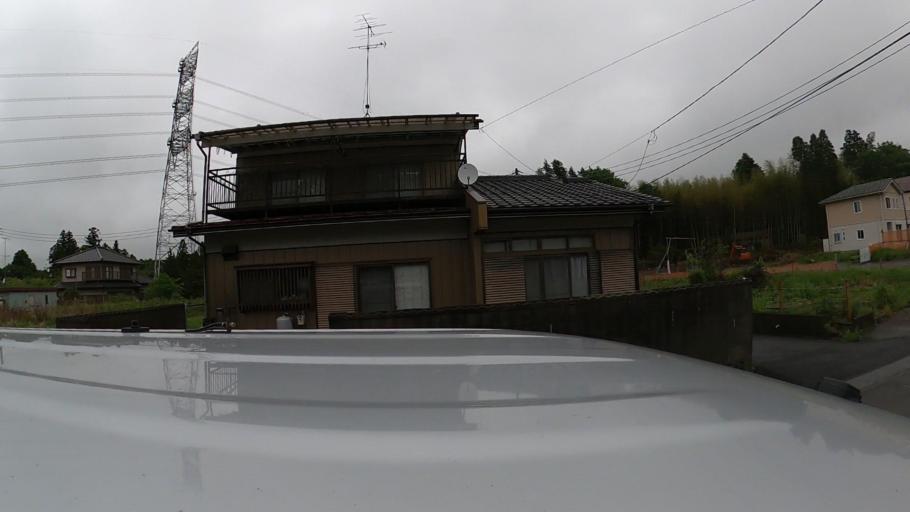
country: JP
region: Ibaraki
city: Ushiku
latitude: 36.0035
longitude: 140.1172
